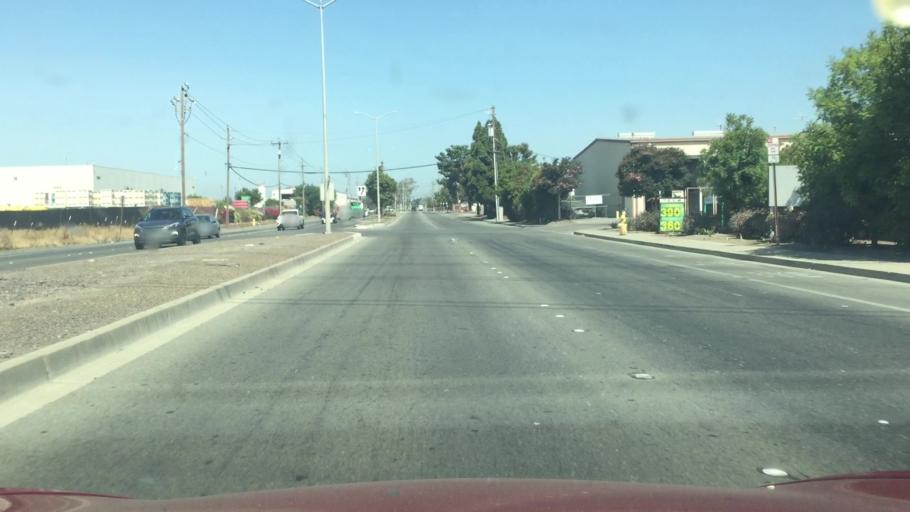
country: US
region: California
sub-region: Alameda County
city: Fremont
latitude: 37.5046
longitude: -121.9822
